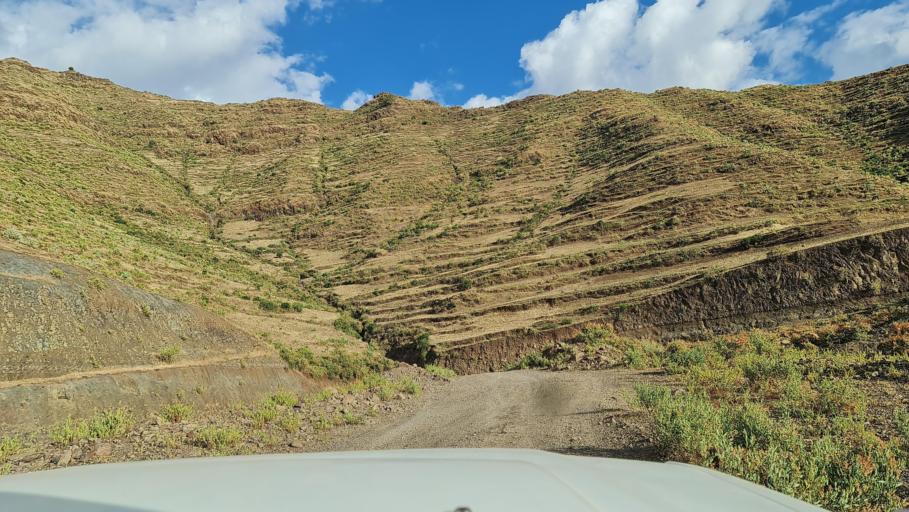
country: ET
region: Amhara
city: Debark'
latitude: 13.0493
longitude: 38.0212
